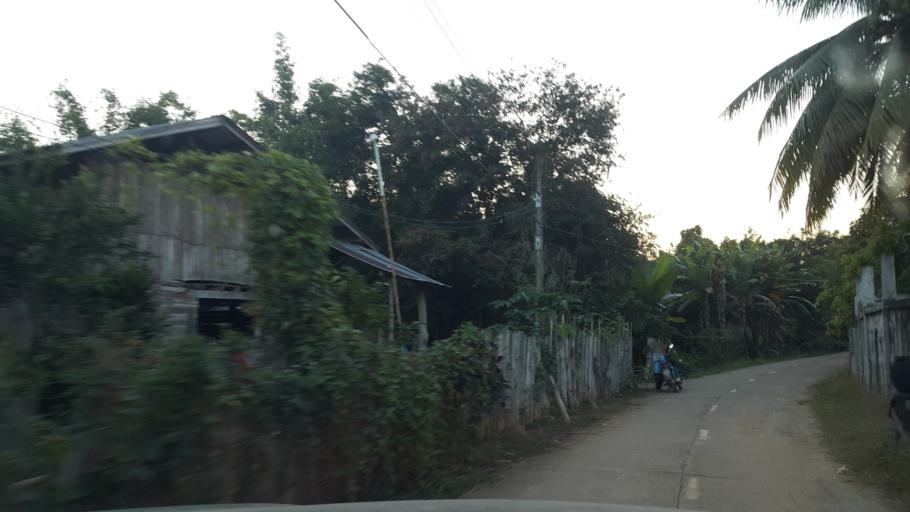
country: TH
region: Phrae
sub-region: Amphoe Wang Chin
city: Wang Chin
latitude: 17.8748
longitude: 99.6219
